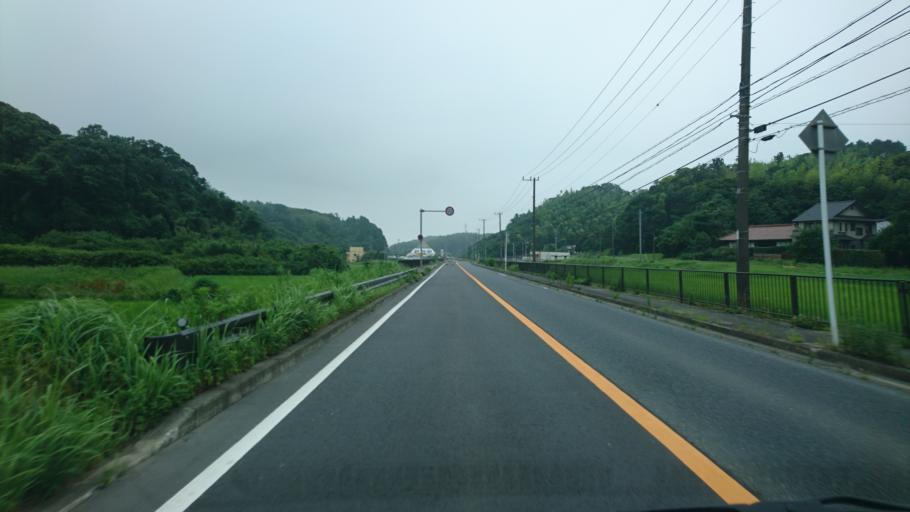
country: JP
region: Chiba
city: Kimitsu
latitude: 35.2747
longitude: 139.9034
